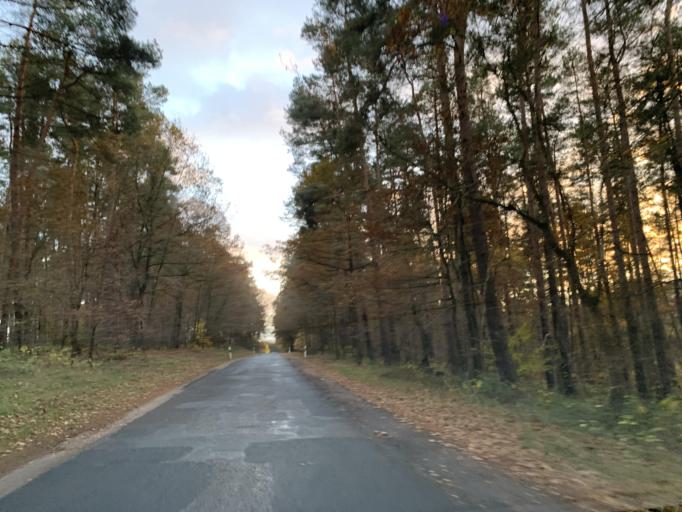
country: DE
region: Mecklenburg-Vorpommern
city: Blankensee
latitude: 53.3911
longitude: 13.2634
